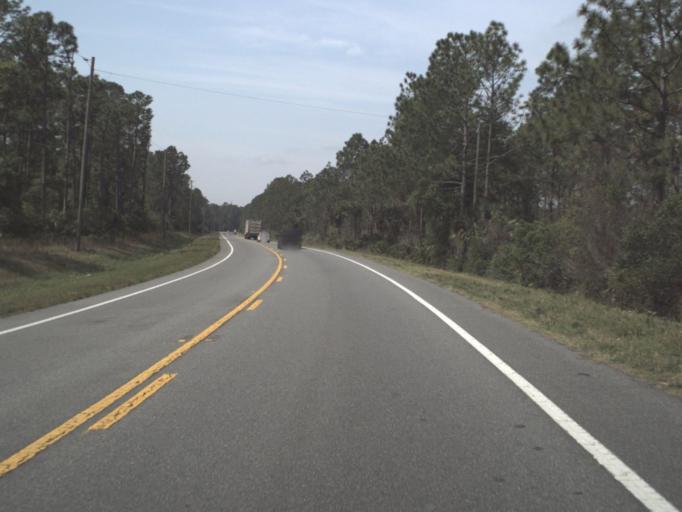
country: US
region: Florida
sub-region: Lake County
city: Astor
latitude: 29.1617
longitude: -81.5514
